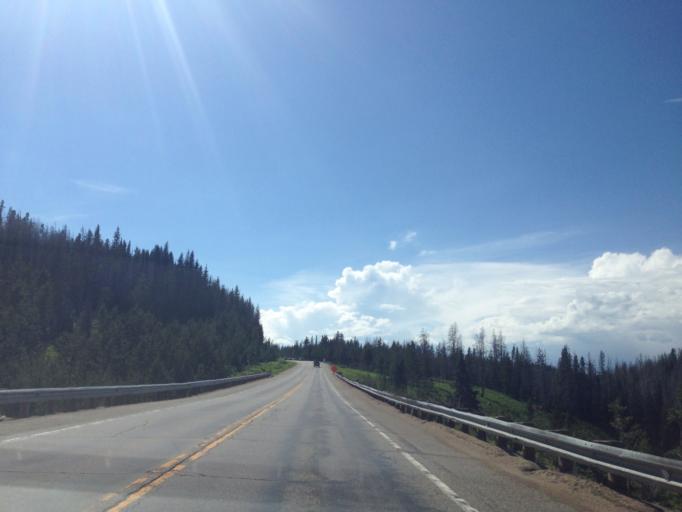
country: US
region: Colorado
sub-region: Routt County
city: Steamboat Springs
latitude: 40.3823
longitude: -106.6914
